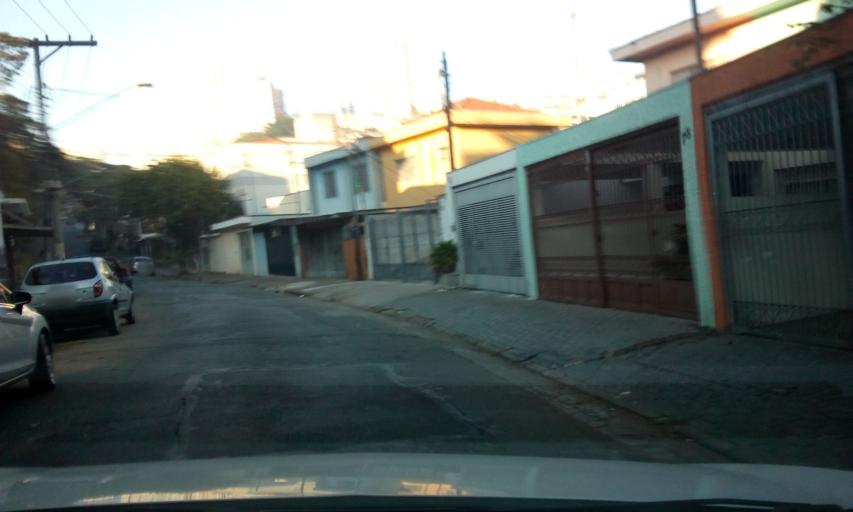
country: BR
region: Sao Paulo
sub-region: Sao Paulo
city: Sao Paulo
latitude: -23.5389
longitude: -46.6925
